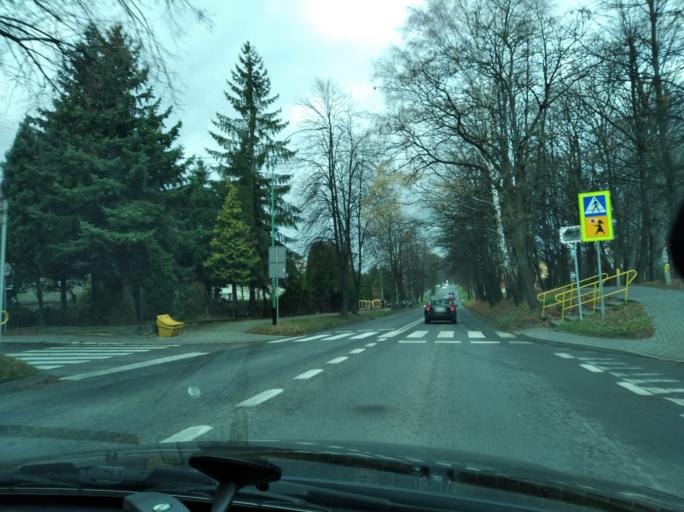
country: PL
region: Subcarpathian Voivodeship
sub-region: Powiat lancucki
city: Lancut
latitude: 50.0723
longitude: 22.2371
